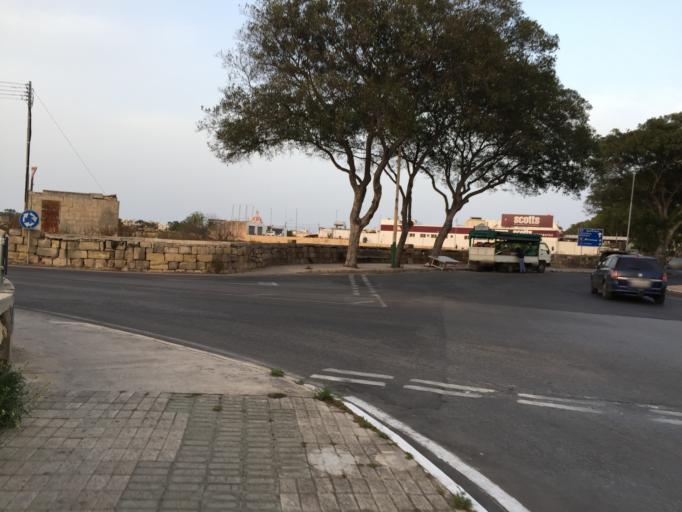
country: MT
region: Haz-Zabbar
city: Zabbar
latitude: 35.8722
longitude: 14.5268
